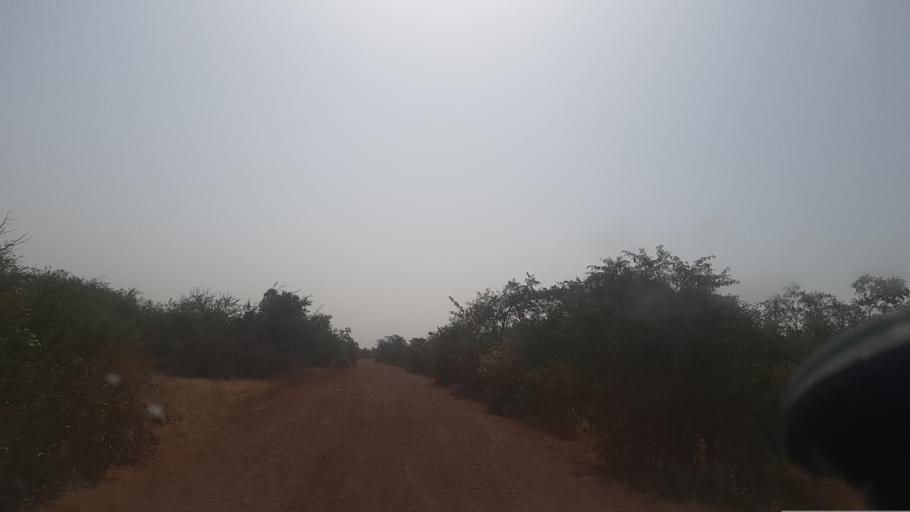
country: ML
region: Segou
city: Baroueli
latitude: 13.0686
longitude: -6.4795
